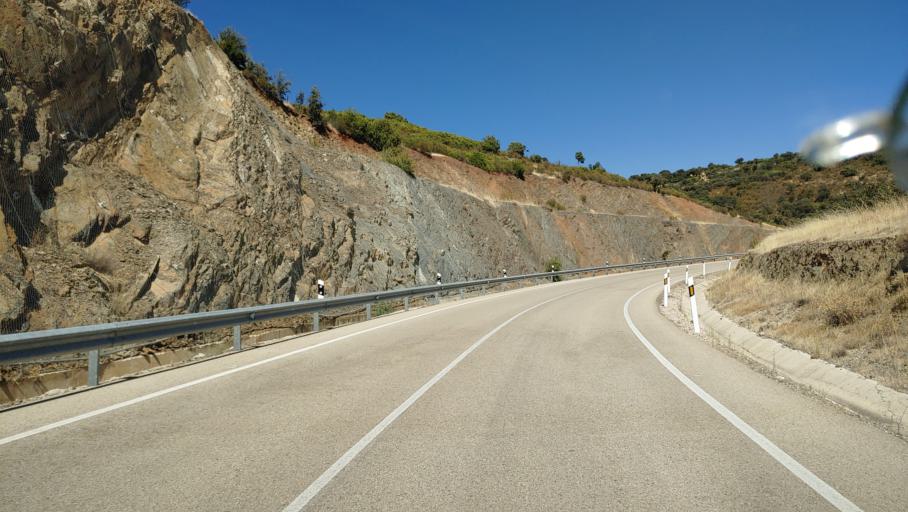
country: ES
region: Andalusia
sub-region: Provincia de Jaen
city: Genave
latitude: 38.4991
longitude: -2.7716
